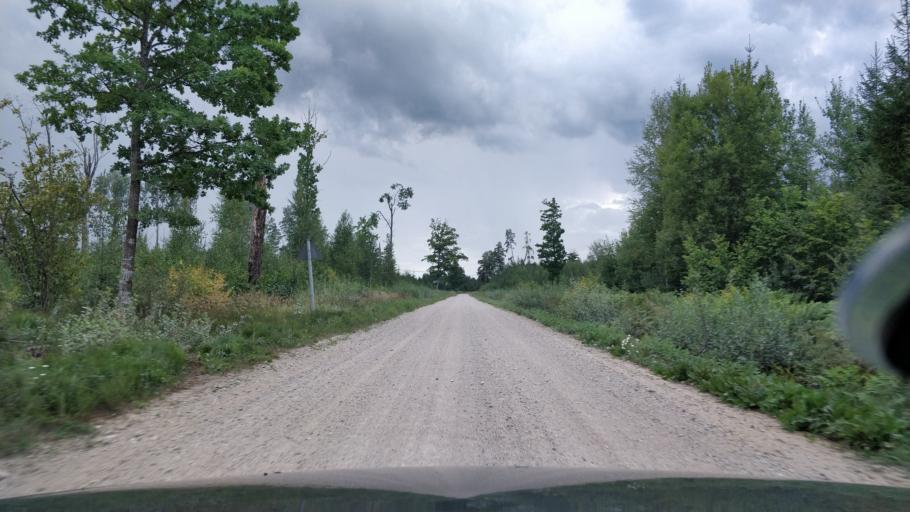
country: LV
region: Kegums
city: Kegums
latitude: 56.8056
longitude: 24.6880
